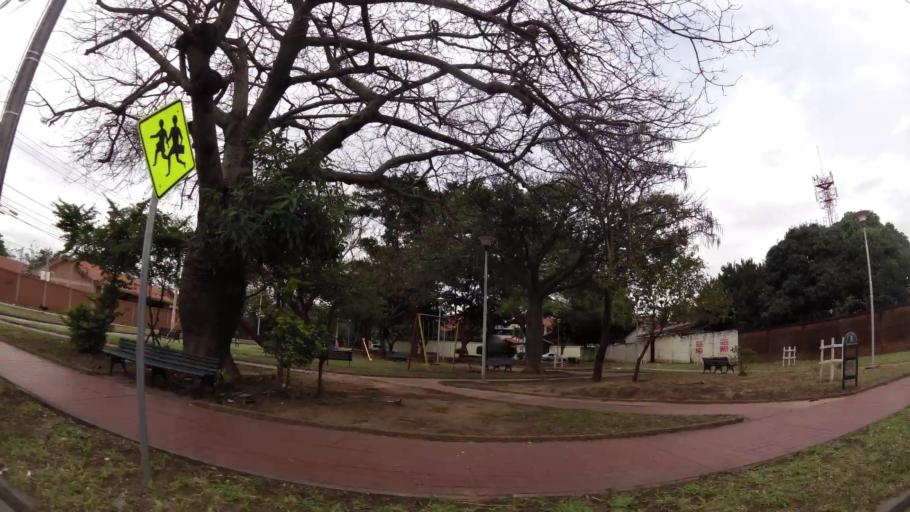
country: BO
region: Santa Cruz
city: Santa Cruz de la Sierra
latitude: -17.7644
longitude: -63.1660
